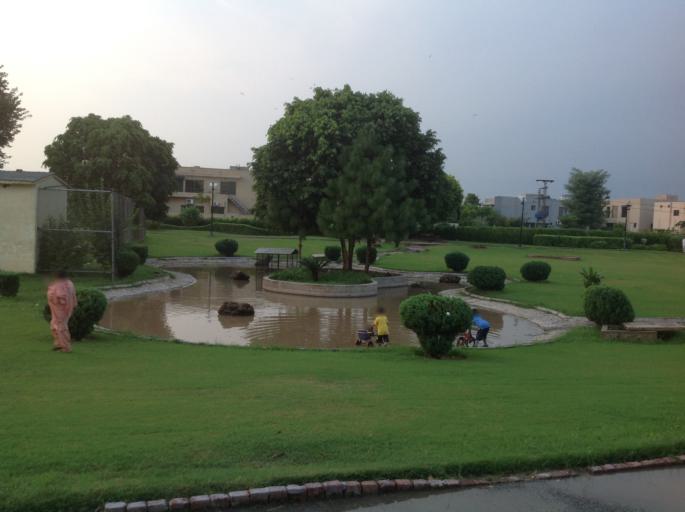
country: PK
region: Punjab
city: Kahna
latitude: 31.4547
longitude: 74.3890
